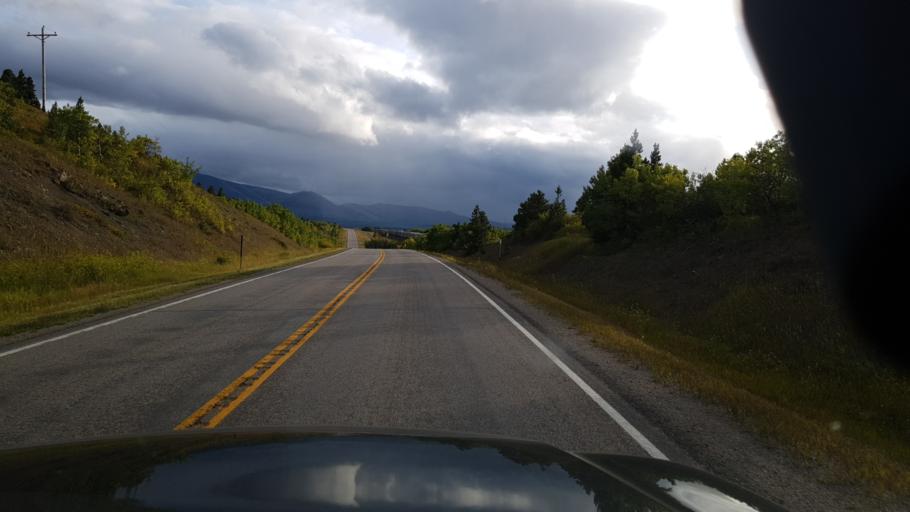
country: US
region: Montana
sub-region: Glacier County
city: South Browning
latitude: 48.3812
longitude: -113.2738
